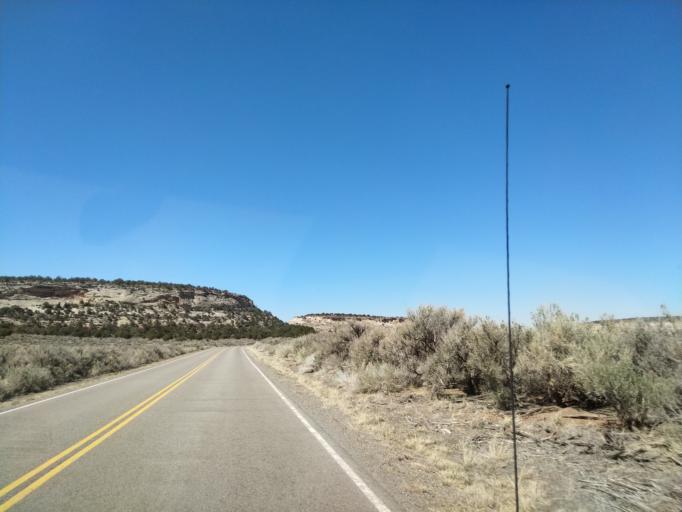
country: US
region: Colorado
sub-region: Mesa County
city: Fruita
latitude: 38.9833
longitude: -108.8043
